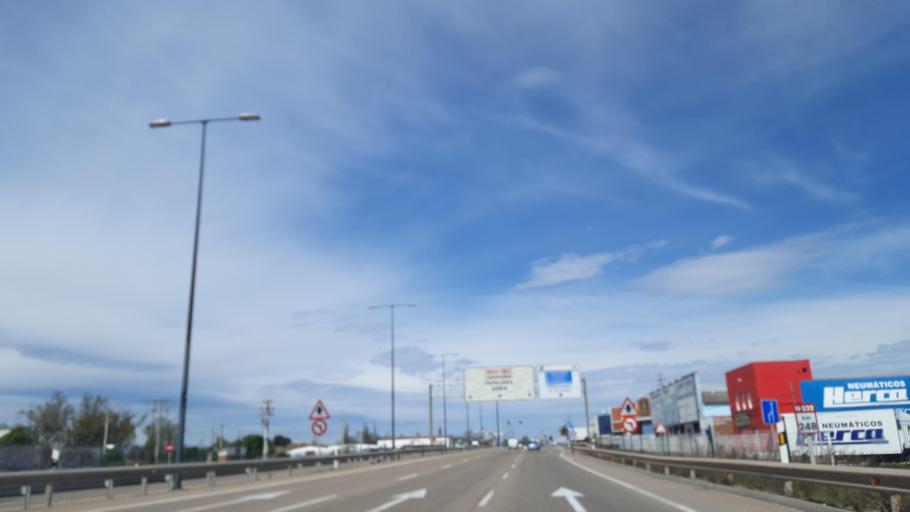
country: ES
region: Aragon
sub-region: Provincia de Zaragoza
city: Utebo
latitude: 41.6876
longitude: -0.9754
